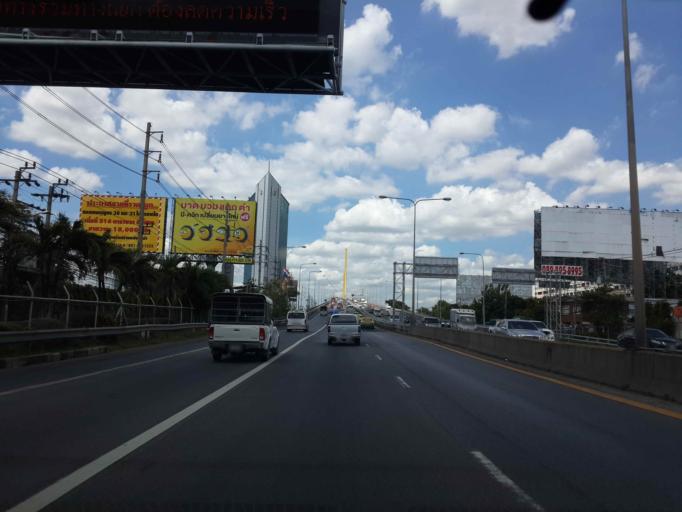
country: TH
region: Bangkok
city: Rat Burana
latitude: 13.6739
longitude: 100.5110
